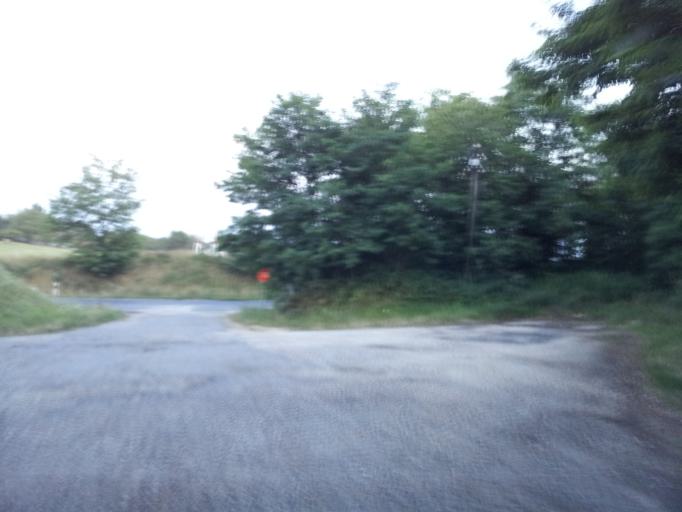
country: HU
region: Zala
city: Zalalovo
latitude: 46.8342
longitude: 16.5859
